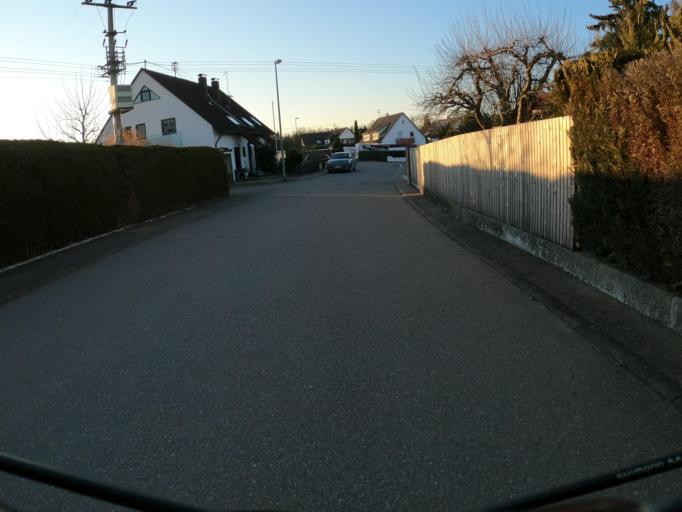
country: DE
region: Bavaria
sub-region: Swabia
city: Nersingen
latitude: 48.4331
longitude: 10.1253
